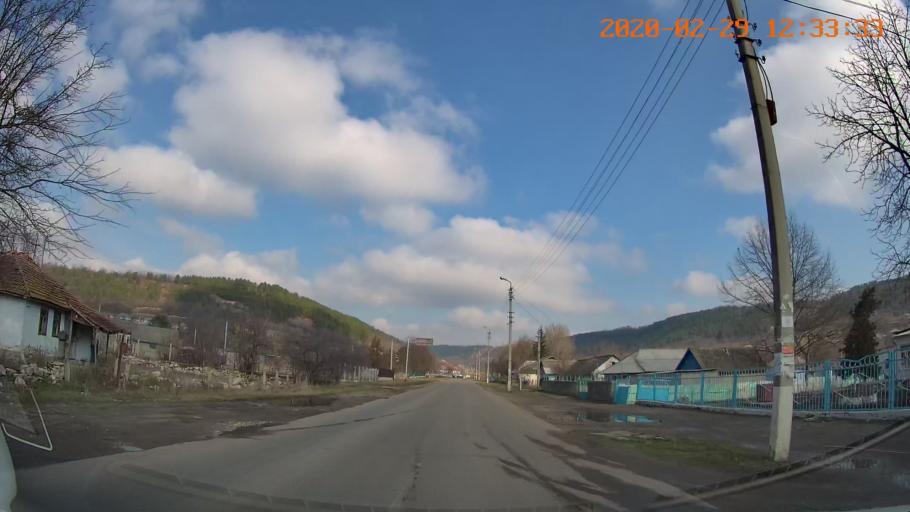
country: MD
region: Telenesti
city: Camenca
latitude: 48.0358
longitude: 28.7053
